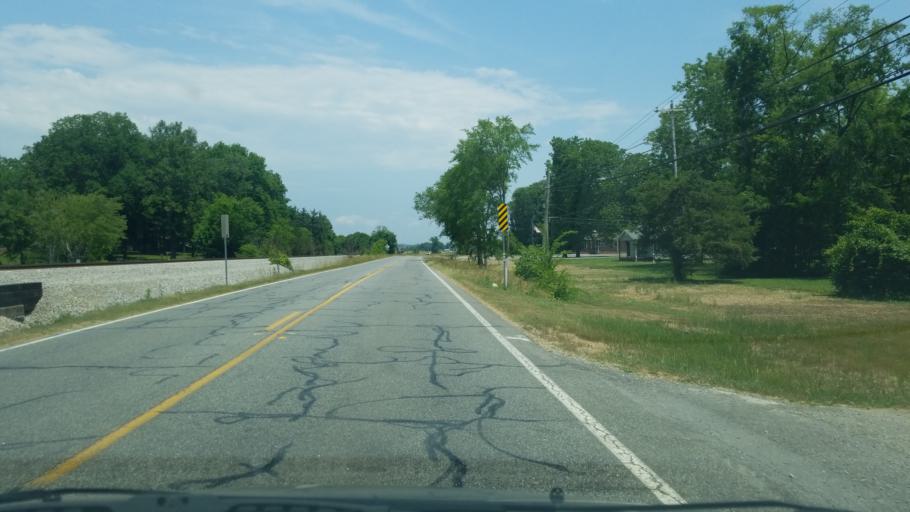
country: US
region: Georgia
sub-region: Catoosa County
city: Ringgold
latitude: 34.9565
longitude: -85.1039
